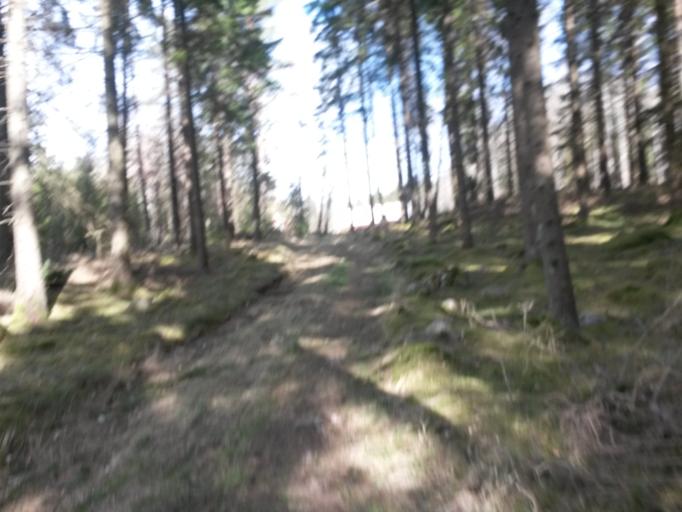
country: SE
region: Vaestra Goetaland
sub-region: Vargarda Kommun
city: Jonstorp
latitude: 57.9546
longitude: 12.6892
